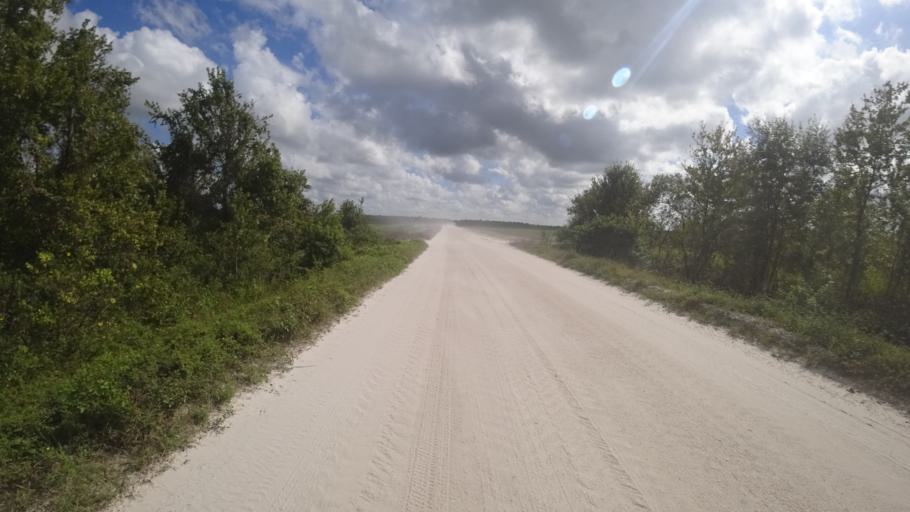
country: US
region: Florida
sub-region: Sarasota County
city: Lake Sarasota
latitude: 27.4131
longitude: -82.1964
